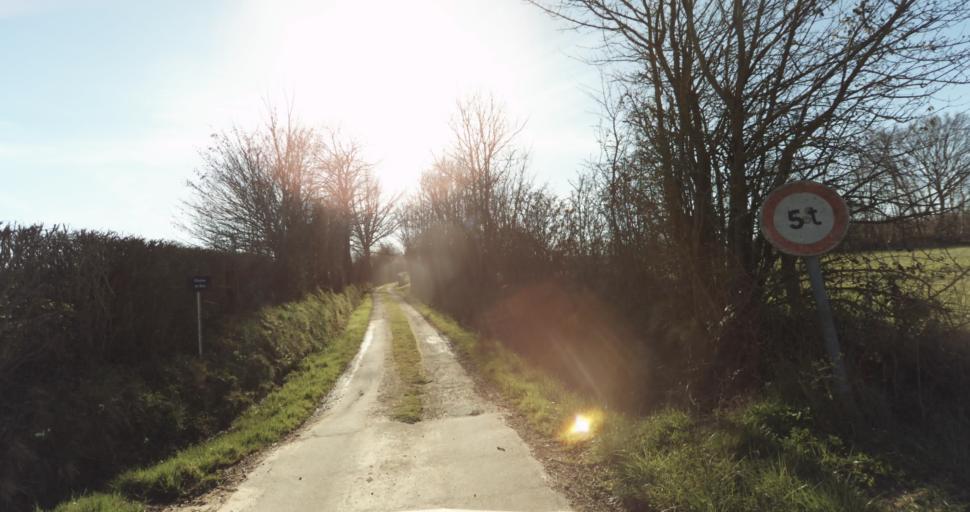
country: FR
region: Lower Normandy
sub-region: Departement du Calvados
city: Saint-Pierre-sur-Dives
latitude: 49.0471
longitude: 0.0495
